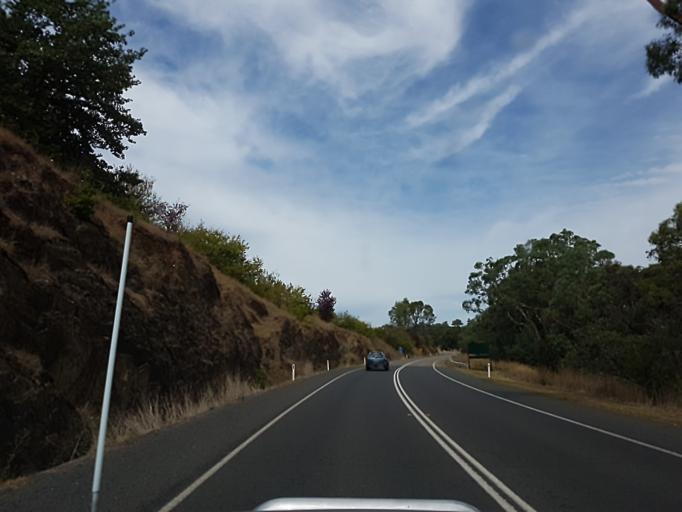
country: AU
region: Victoria
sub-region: Murrindindi
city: Alexandra
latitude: -37.2100
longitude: 145.4360
